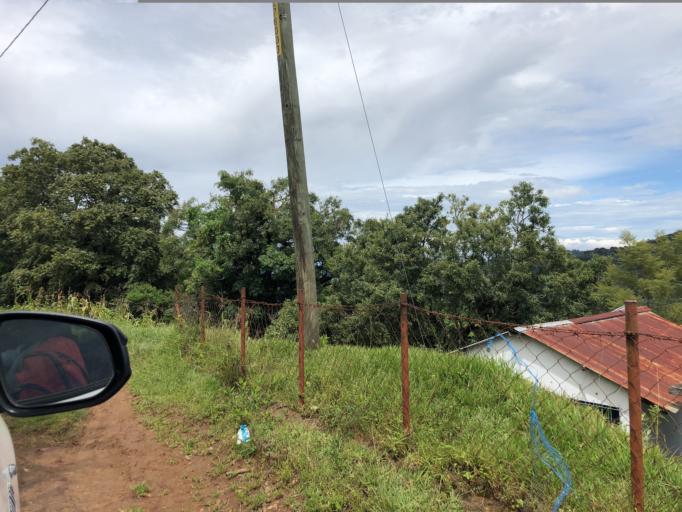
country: GT
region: Guatemala
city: Santa Catarina Pinula
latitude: 14.5315
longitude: -90.4954
